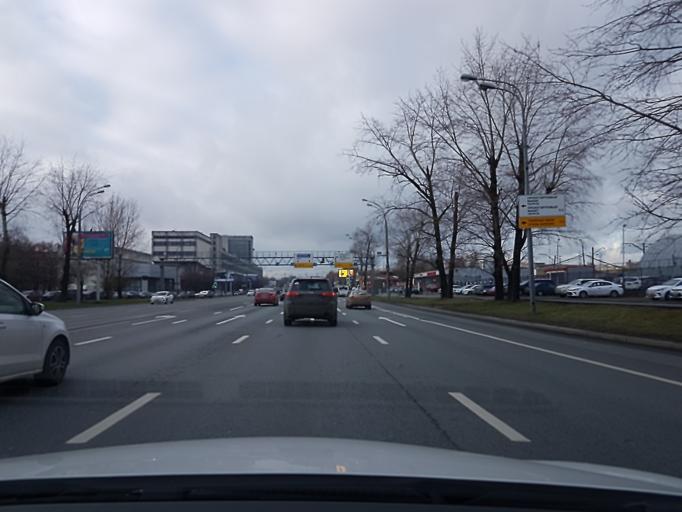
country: RU
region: Moscow
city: Strogino
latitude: 55.8297
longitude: 37.4104
